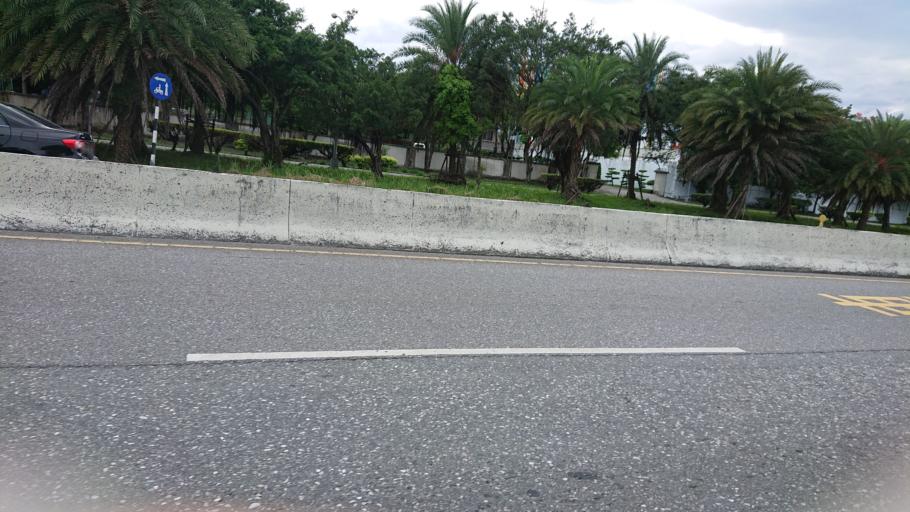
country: TW
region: Taiwan
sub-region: Hualien
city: Hualian
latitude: 23.9367
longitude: 121.5944
